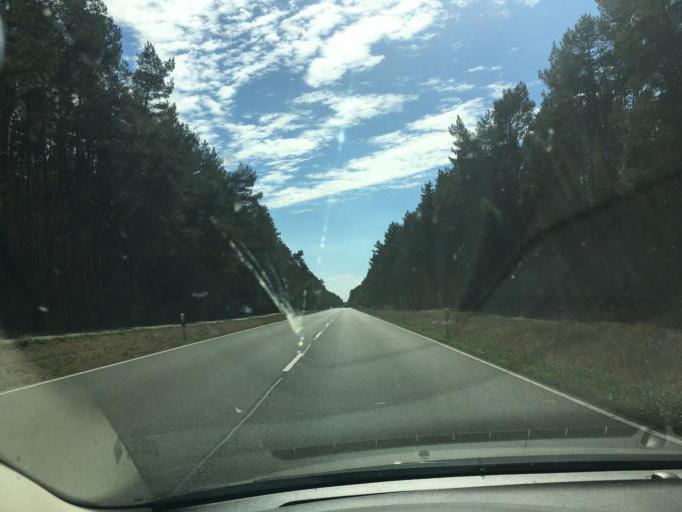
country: DE
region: Saxony-Anhalt
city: Seehausen
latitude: 52.8662
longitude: 11.7315
